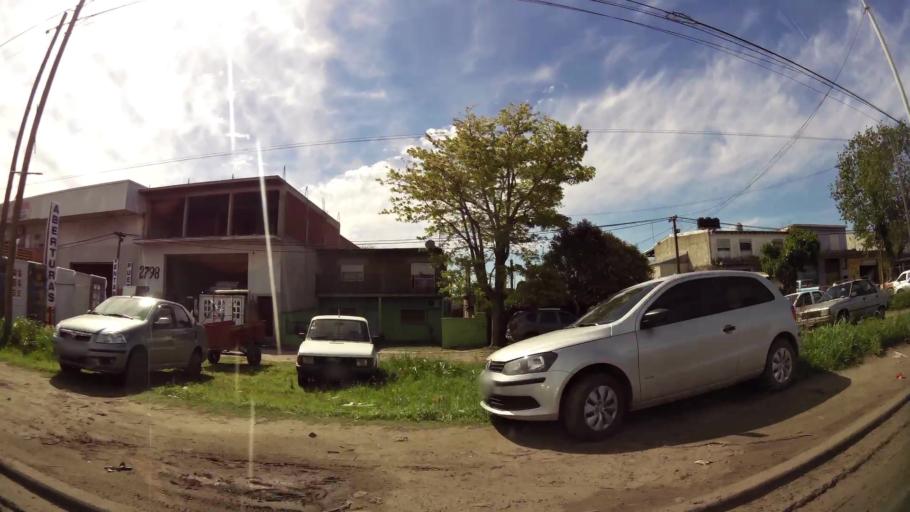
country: AR
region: Buenos Aires
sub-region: Partido de Almirante Brown
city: Adrogue
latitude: -34.7899
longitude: -58.3094
